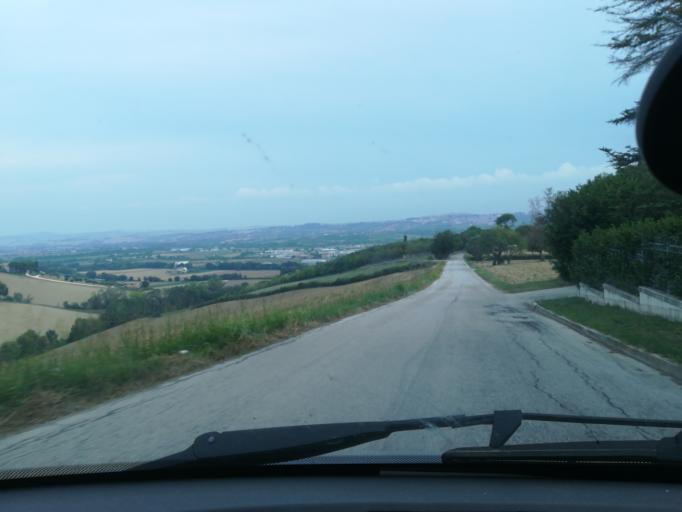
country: IT
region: The Marches
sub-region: Provincia di Macerata
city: Piediripa
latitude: 43.2937
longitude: 13.4875
